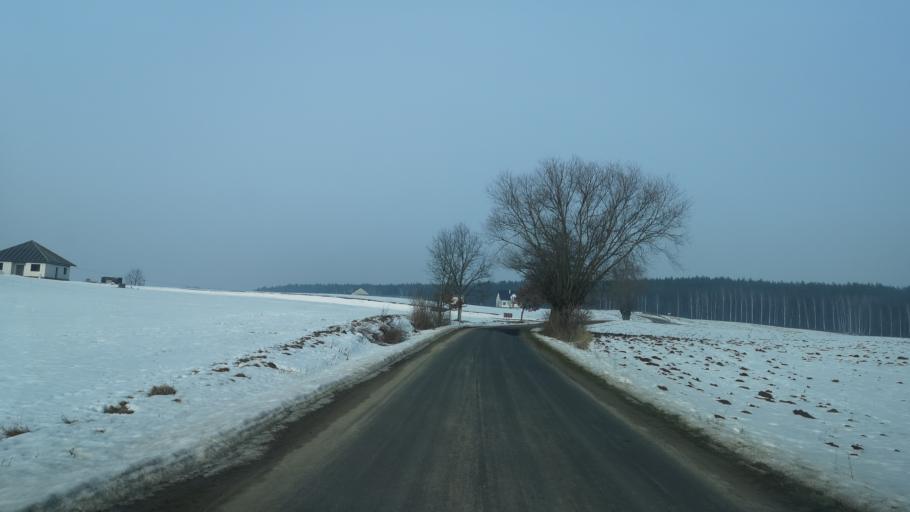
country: PL
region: Warmian-Masurian Voivodeship
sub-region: Powiat nowomiejski
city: Biskupiec
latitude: 53.5408
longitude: 19.3566
